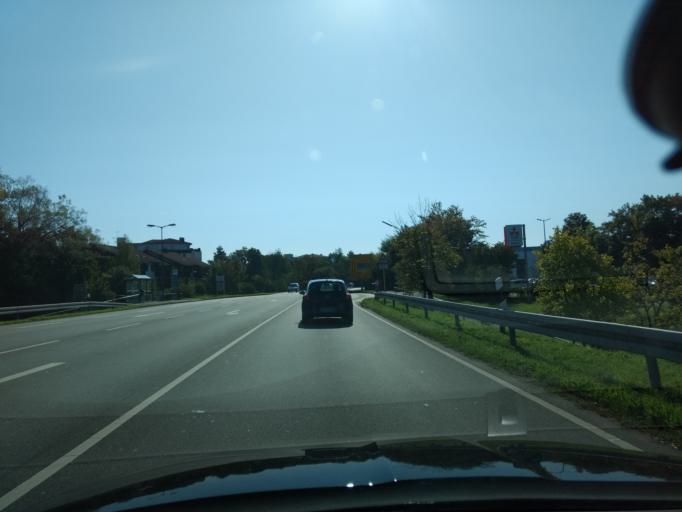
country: DE
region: Bavaria
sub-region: Upper Bavaria
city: Wolfratshausen
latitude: 47.9069
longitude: 11.4307
